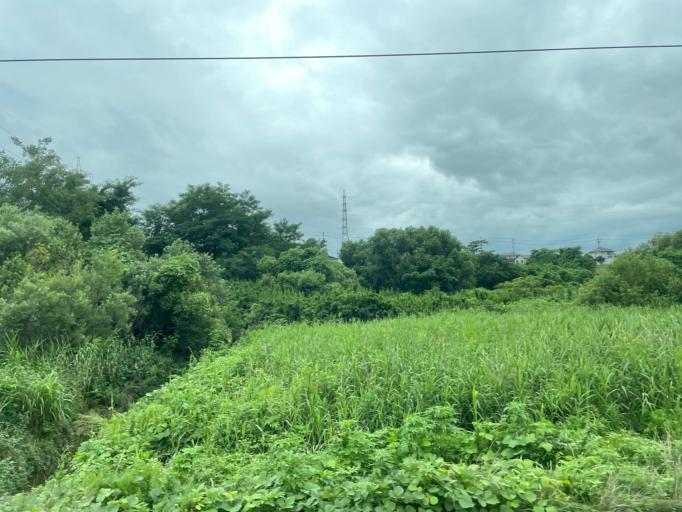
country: JP
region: Fukushima
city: Koriyama
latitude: 37.4515
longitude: 140.3832
